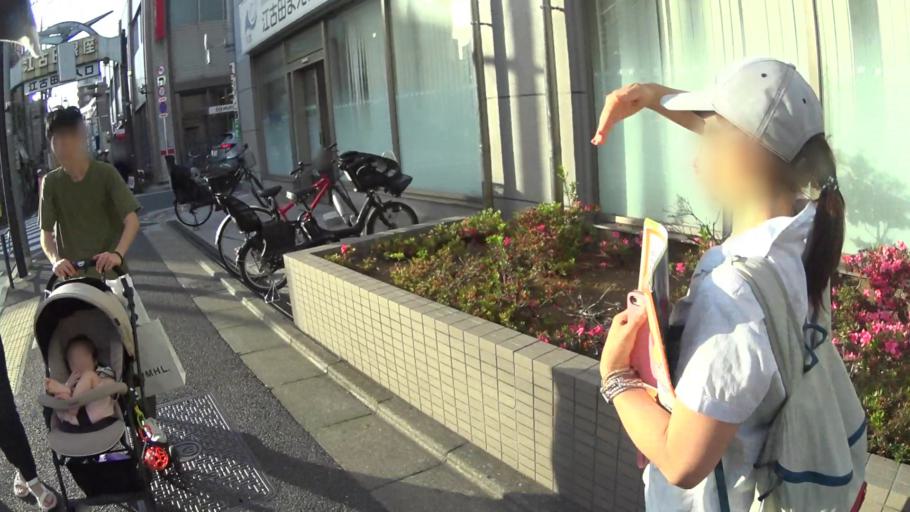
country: JP
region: Tokyo
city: Tokyo
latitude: 35.7361
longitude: 139.6730
